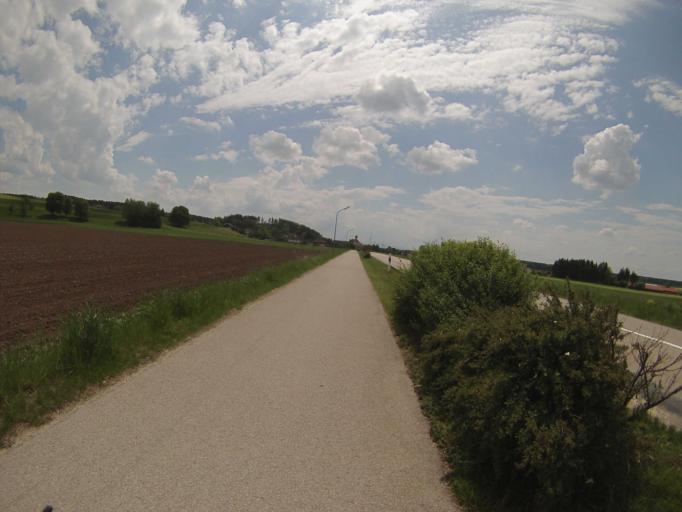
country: DE
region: Bavaria
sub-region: Upper Bavaria
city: Aying
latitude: 47.9657
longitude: 11.7775
